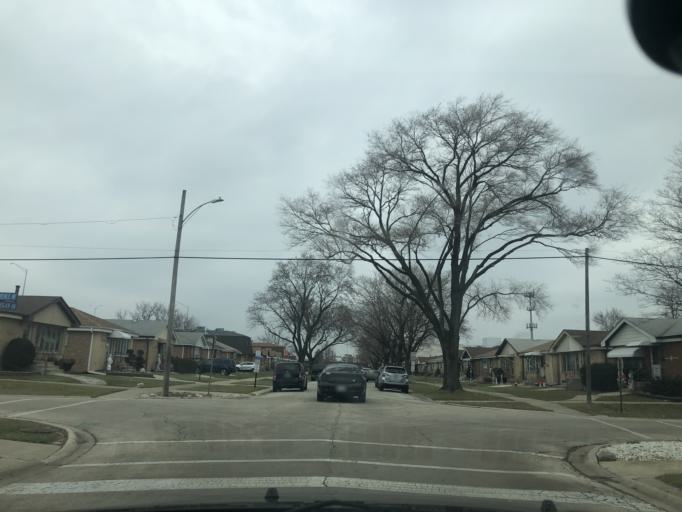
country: US
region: Illinois
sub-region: Cook County
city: Schiller Park
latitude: 41.9711
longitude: -87.8687
